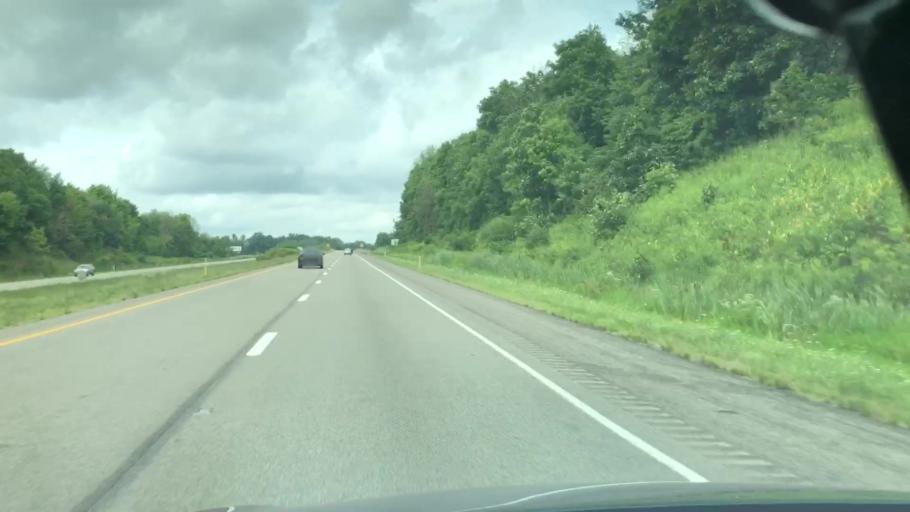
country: US
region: Pennsylvania
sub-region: Crawford County
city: Meadville
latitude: 41.5629
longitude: -80.1815
